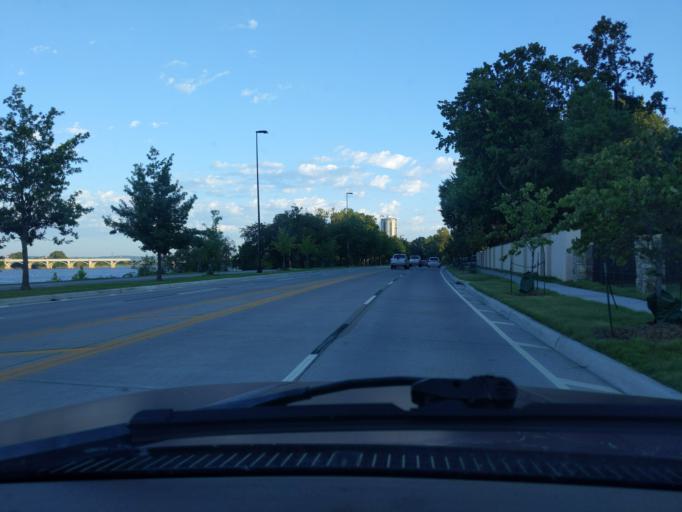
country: US
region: Oklahoma
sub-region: Tulsa County
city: Tulsa
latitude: 36.1261
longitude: -95.9870
